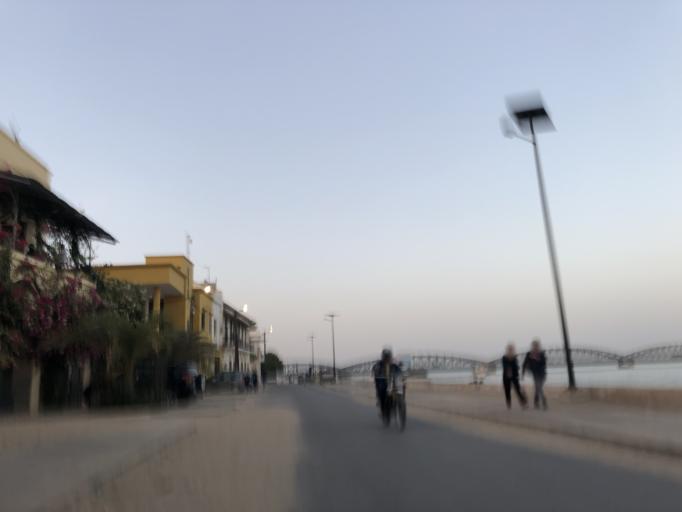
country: SN
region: Saint-Louis
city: Saint-Louis
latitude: 16.0237
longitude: -16.5038
